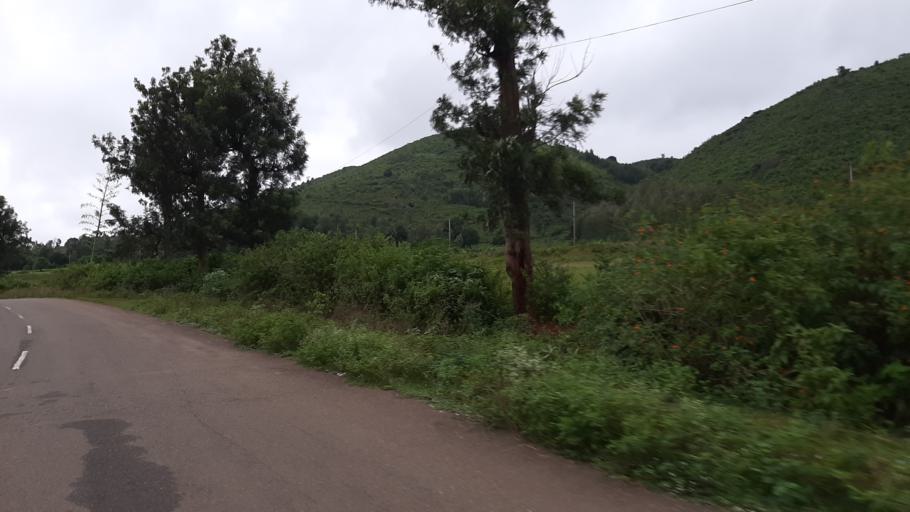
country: IN
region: Andhra Pradesh
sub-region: Vizianagaram District
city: Salur
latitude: 18.2901
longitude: 82.9251
